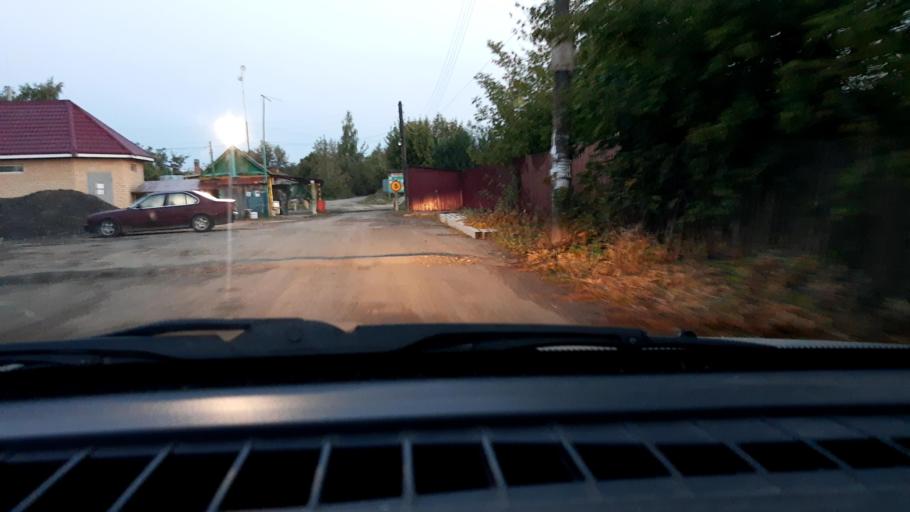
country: RU
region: Nizjnij Novgorod
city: Gorbatovka
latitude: 56.2621
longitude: 43.8250
